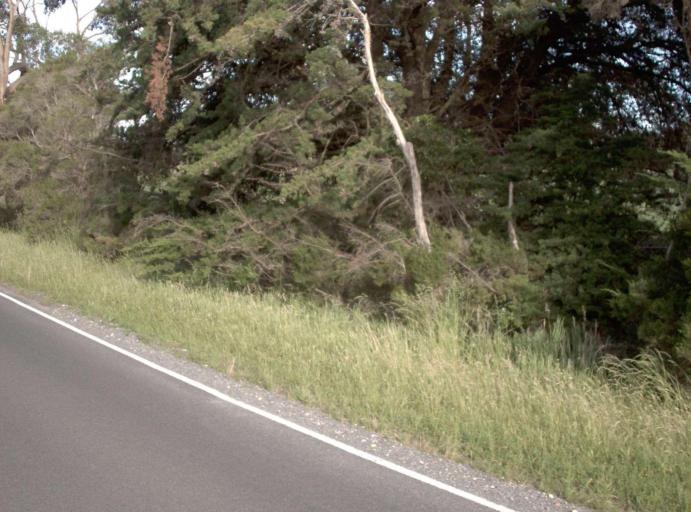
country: AU
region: Victoria
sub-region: Bass Coast
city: North Wonthaggi
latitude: -38.5998
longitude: 145.7783
